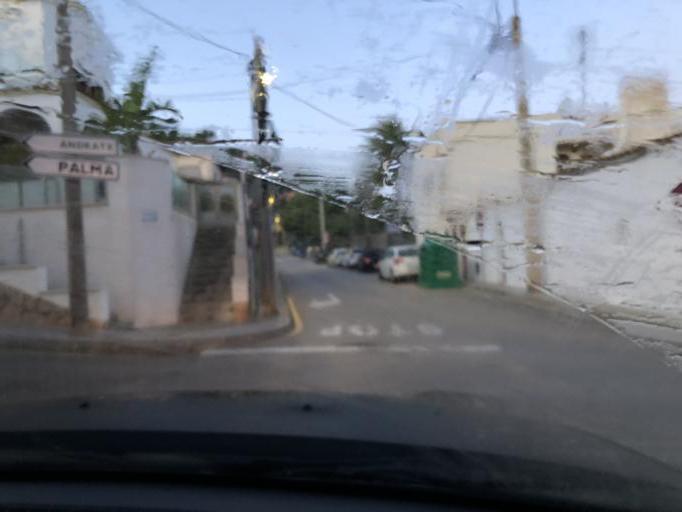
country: ES
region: Balearic Islands
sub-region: Illes Balears
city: Camp de Mar
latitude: 39.5423
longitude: 2.3855
